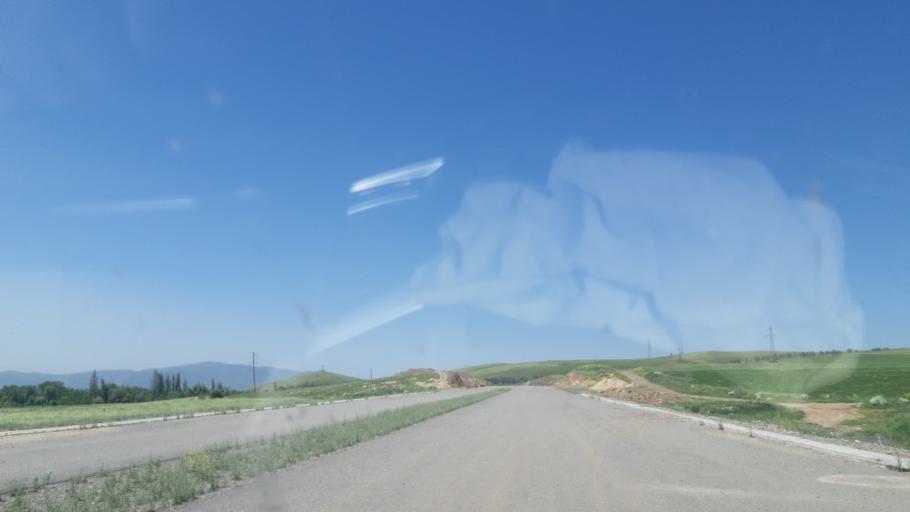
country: KZ
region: Ongtustik Qazaqstan
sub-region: Tulkibas Audany
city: Zhabagly
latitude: 42.5176
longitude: 70.5471
